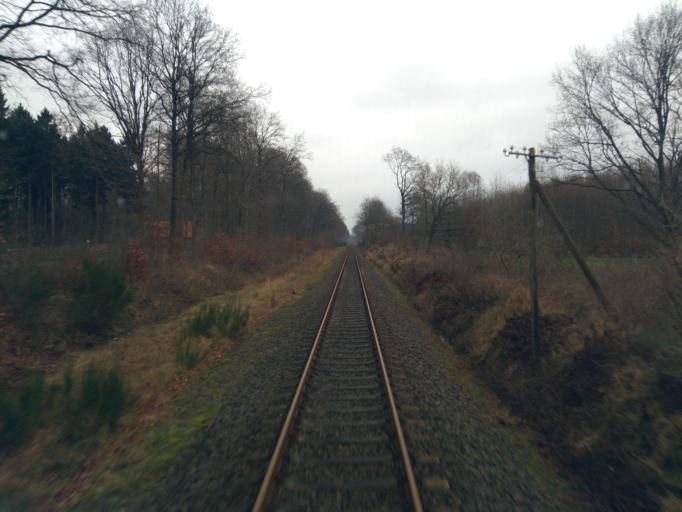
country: DE
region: Lower Saxony
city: Wittorf
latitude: 52.9587
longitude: 9.4727
